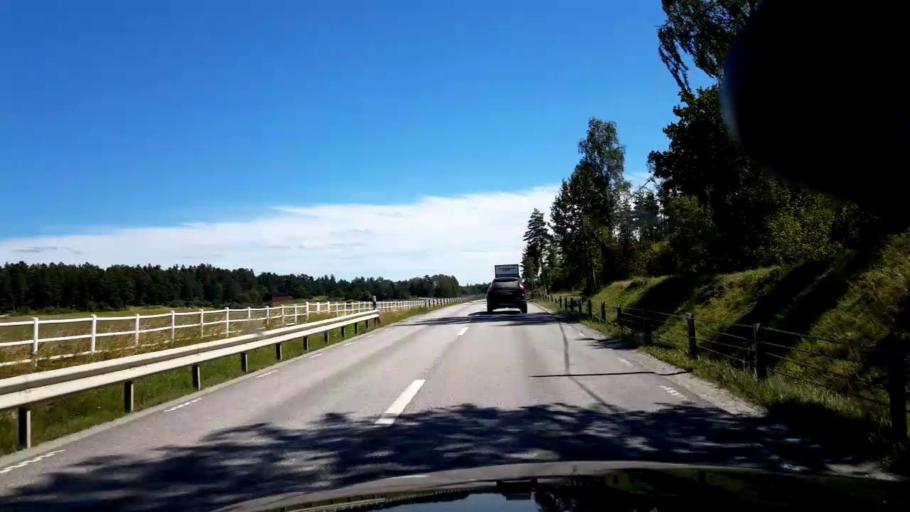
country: SE
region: Stockholm
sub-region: Sigtuna Kommun
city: Sigtuna
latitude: 59.6460
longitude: 17.6227
